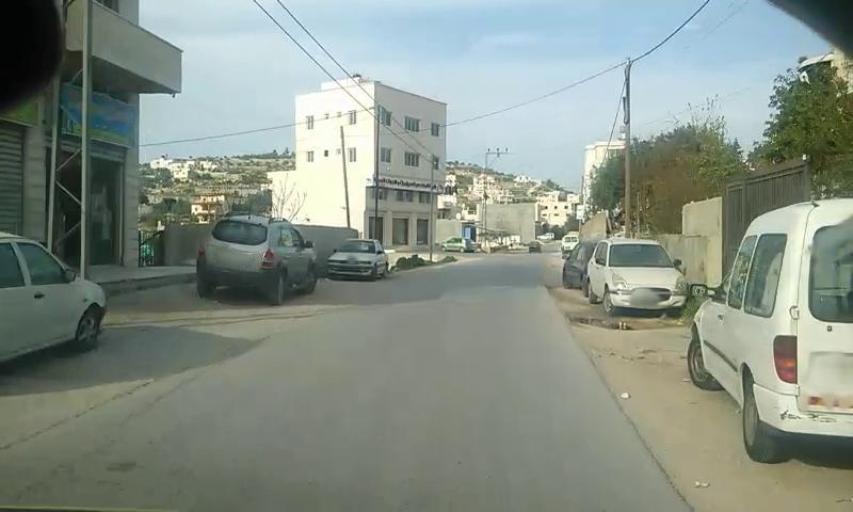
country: PS
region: West Bank
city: Tarqumya
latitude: 31.5799
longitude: 35.0179
